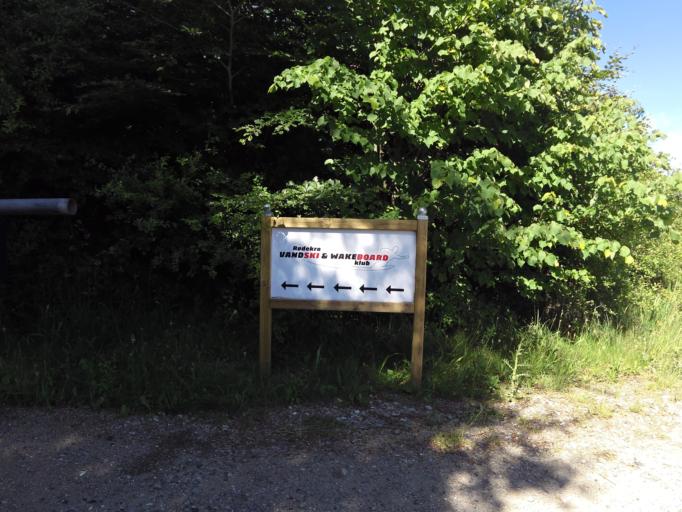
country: DK
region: South Denmark
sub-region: Aabenraa Kommune
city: Rodekro
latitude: 55.0602
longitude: 9.3000
